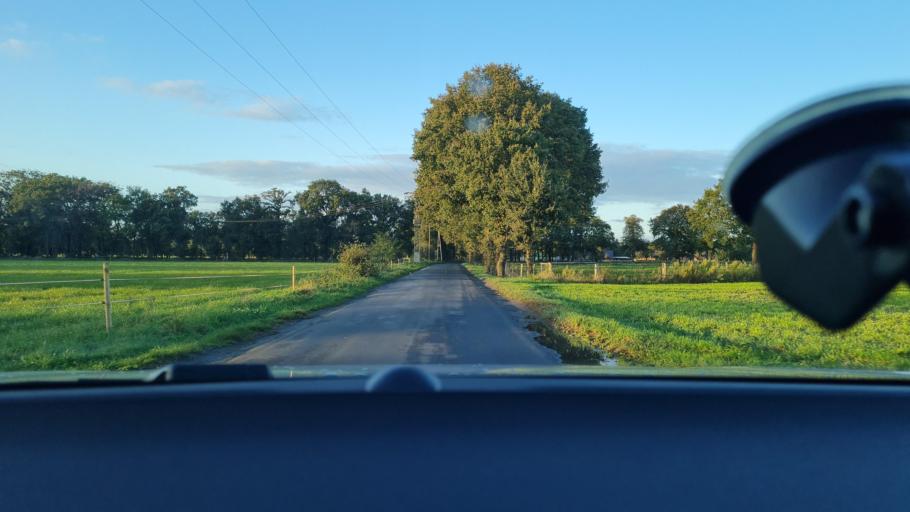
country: DE
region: North Rhine-Westphalia
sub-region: Regierungsbezirk Dusseldorf
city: Dinslaken
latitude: 51.5979
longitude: 6.7338
